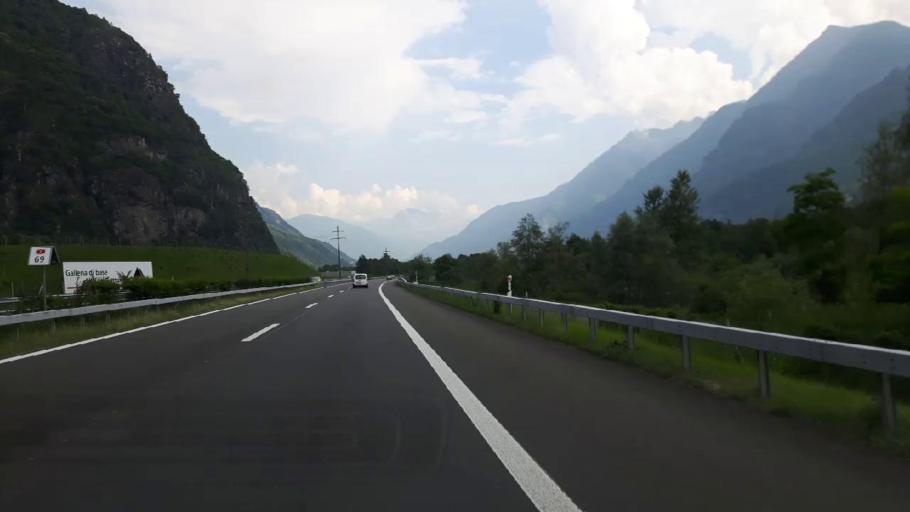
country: CH
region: Ticino
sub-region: Riviera District
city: Lodrino
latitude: 46.3272
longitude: 8.9789
